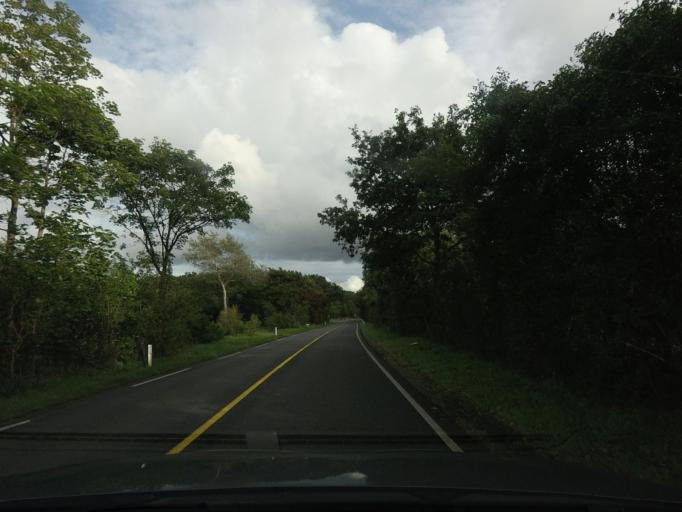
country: NL
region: North Holland
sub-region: Gemeente Bloemendaal
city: Bloemendaal
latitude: 52.3966
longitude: 4.5862
